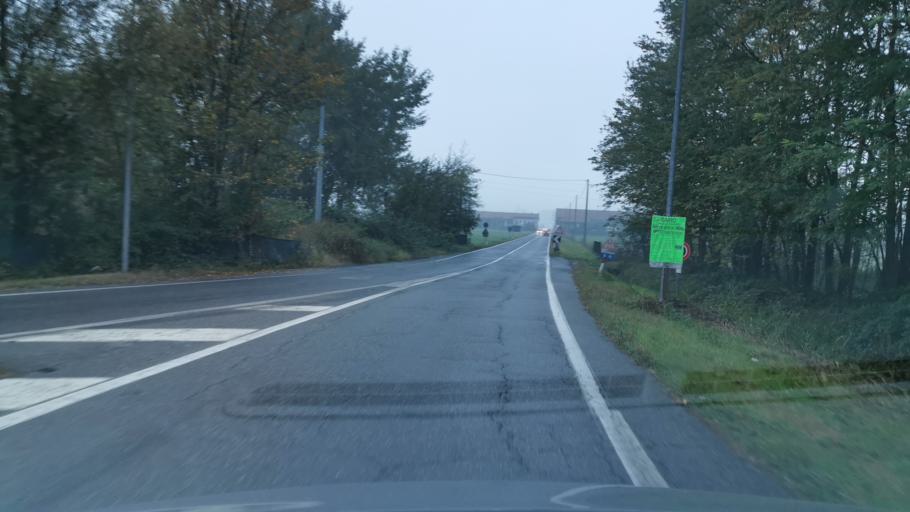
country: IT
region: Piedmont
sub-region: Provincia di Torino
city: Ciconio
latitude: 45.3446
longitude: 7.7654
